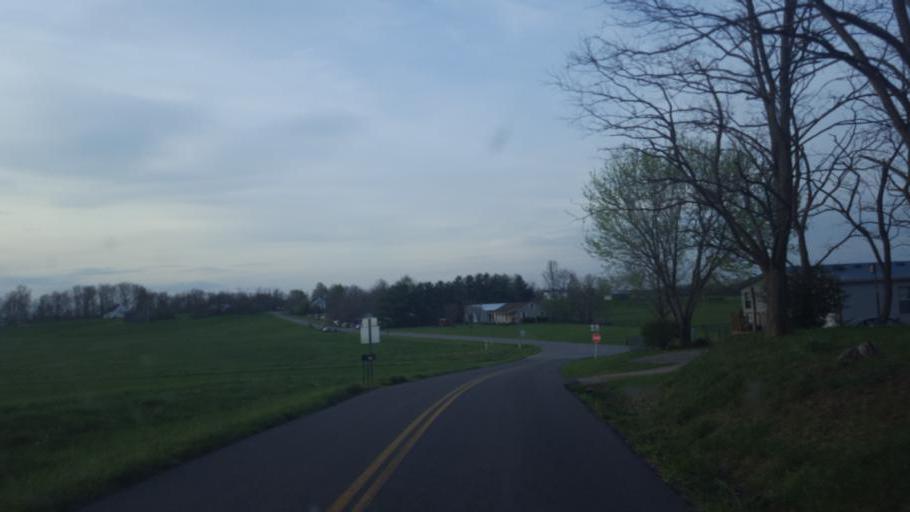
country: US
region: Kentucky
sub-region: Metcalfe County
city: Edmonton
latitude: 37.1363
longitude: -85.6935
